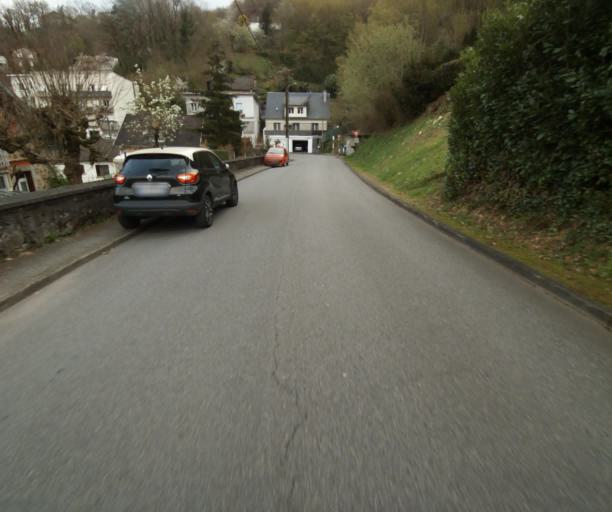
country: FR
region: Limousin
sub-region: Departement de la Correze
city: Tulle
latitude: 45.2606
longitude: 1.7629
